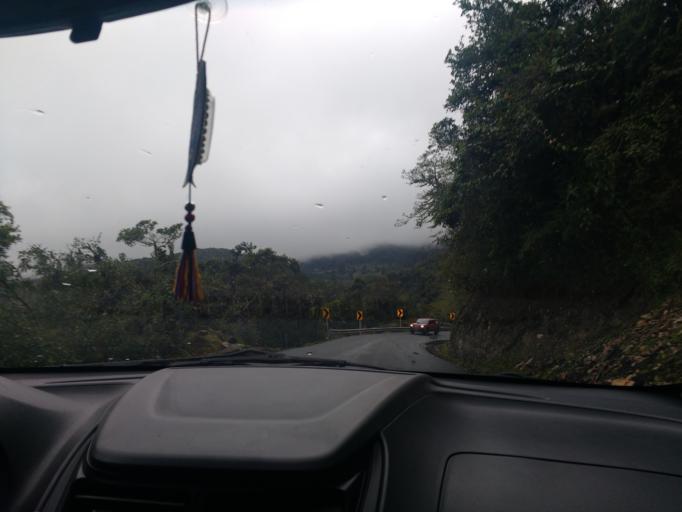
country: CO
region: Cundinamarca
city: Choachi
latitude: 4.5630
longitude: -73.9578
